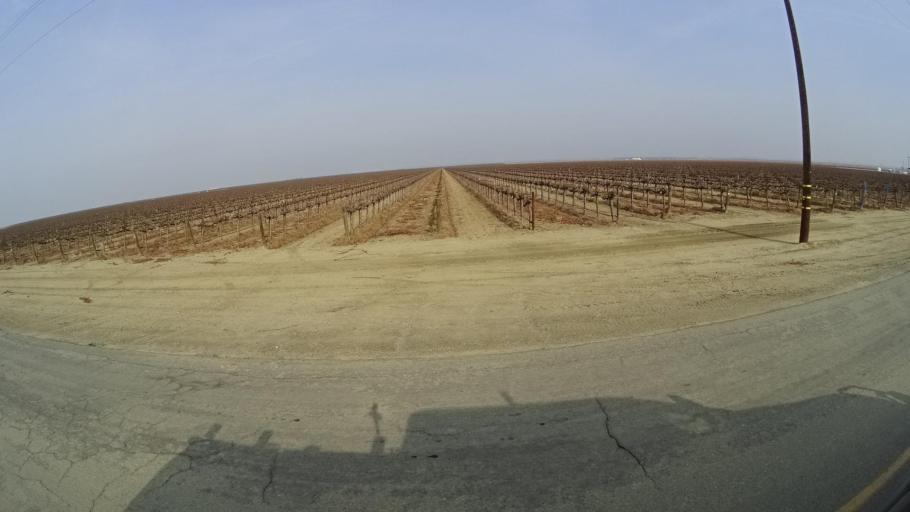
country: US
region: California
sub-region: Kern County
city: Greenfield
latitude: 35.0765
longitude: -119.0858
